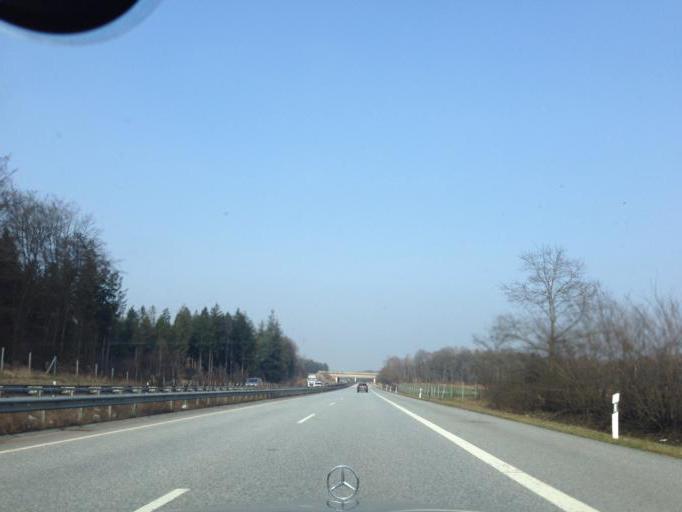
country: DE
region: Schleswig-Holstein
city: Negernbotel
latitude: 53.9911
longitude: 10.2442
